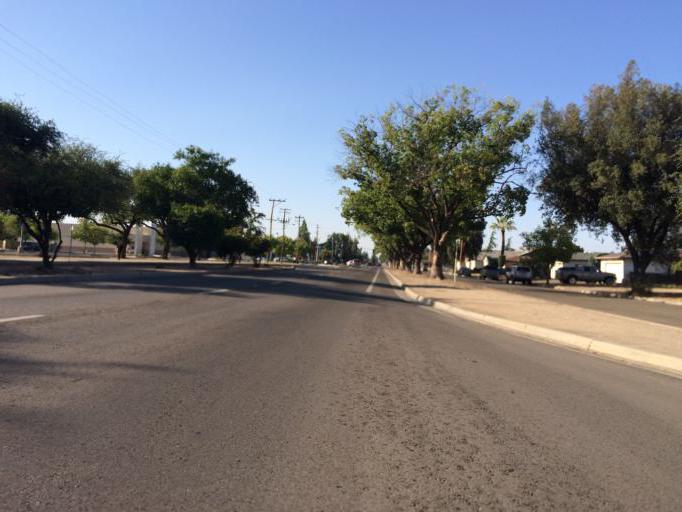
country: US
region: California
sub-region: Fresno County
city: Tarpey Village
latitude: 36.7993
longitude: -119.7541
